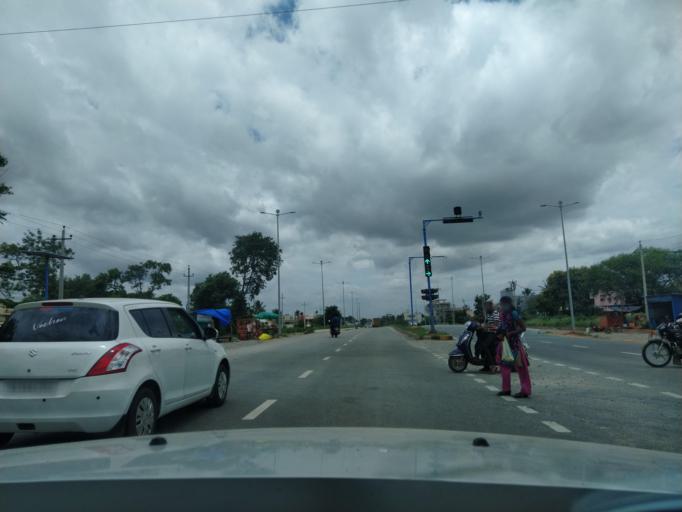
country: IN
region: Karnataka
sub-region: Tumkur
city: Tumkur
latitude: 13.3087
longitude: 77.1428
